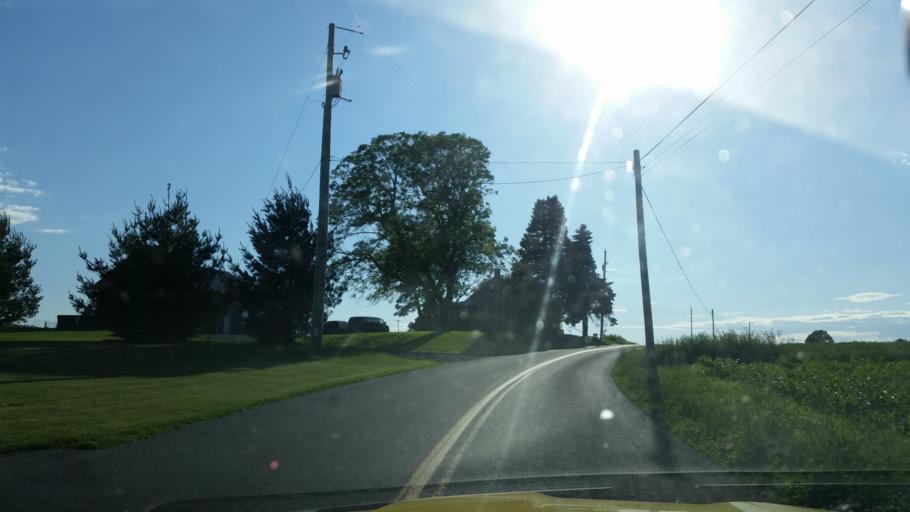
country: US
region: Pennsylvania
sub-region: Lebanon County
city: Avon
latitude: 40.3238
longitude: -76.3562
